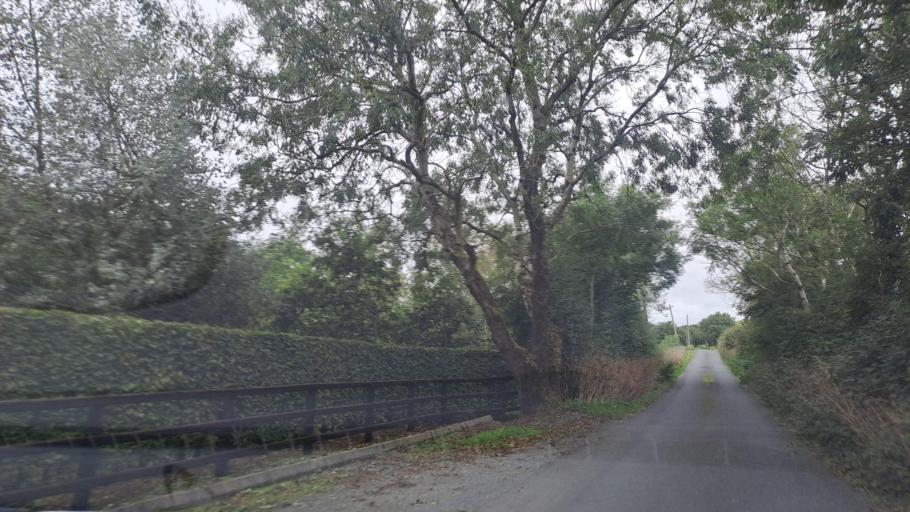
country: IE
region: Ulster
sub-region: An Cabhan
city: Kingscourt
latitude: 54.0049
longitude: -6.8611
